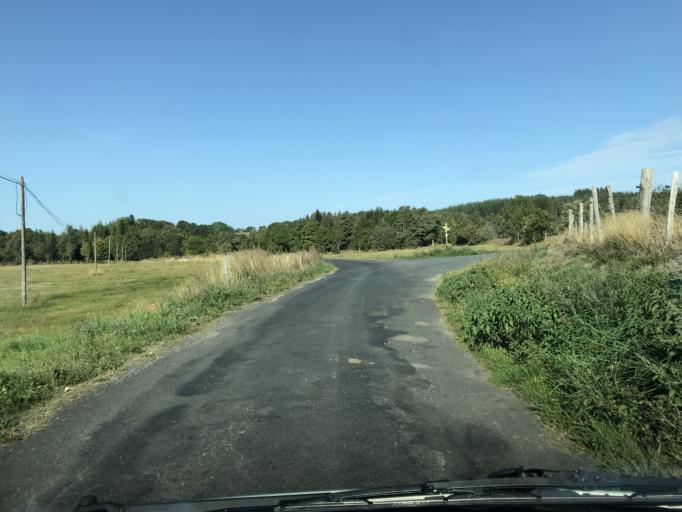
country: FR
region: Rhone-Alpes
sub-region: Departement de l'Ardeche
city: Saint-Agreve
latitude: 45.0266
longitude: 4.4344
